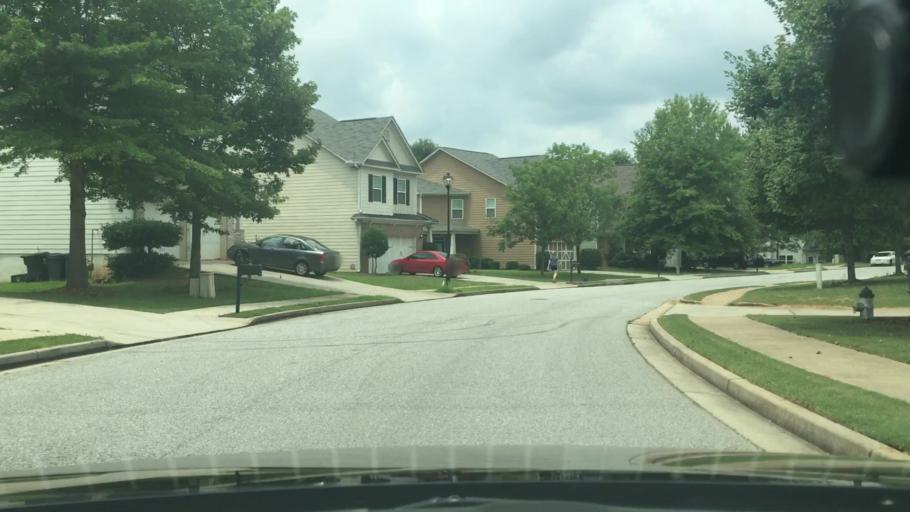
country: US
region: Georgia
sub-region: Coweta County
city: East Newnan
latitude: 33.3814
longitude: -84.7478
